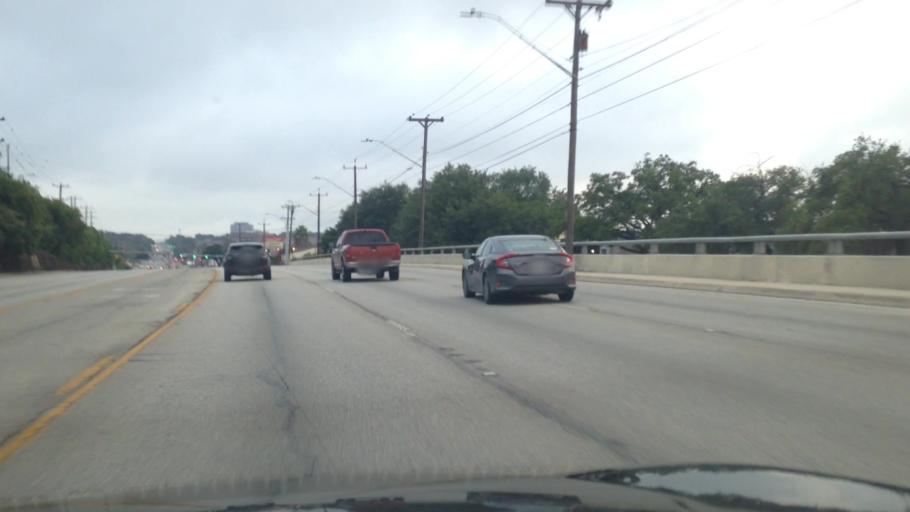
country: US
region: Texas
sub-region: Bexar County
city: Balcones Heights
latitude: 29.4987
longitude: -98.5568
